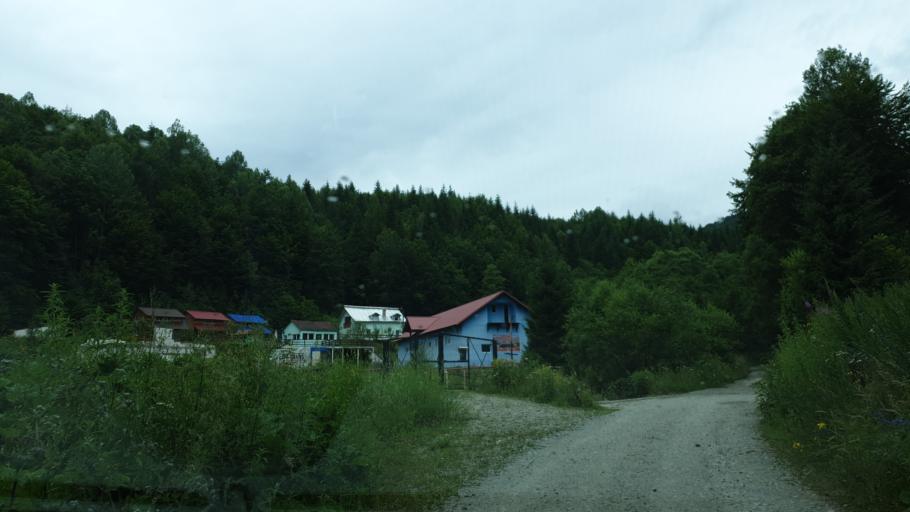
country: RO
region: Hunedoara
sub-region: Comuna Uricani
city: Uricani
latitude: 45.3015
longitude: 22.9909
